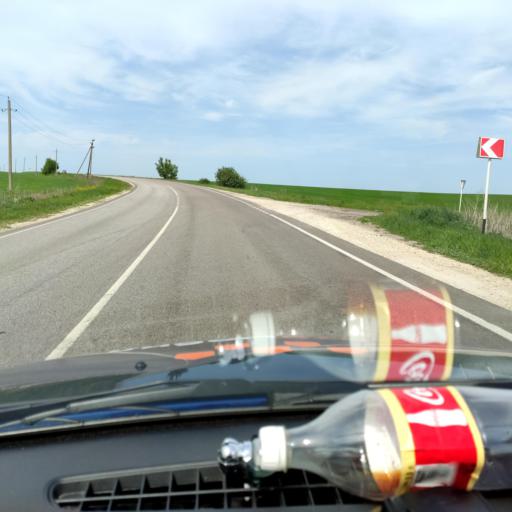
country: RU
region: Voronezj
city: Novaya Usman'
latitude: 51.5559
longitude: 39.3758
